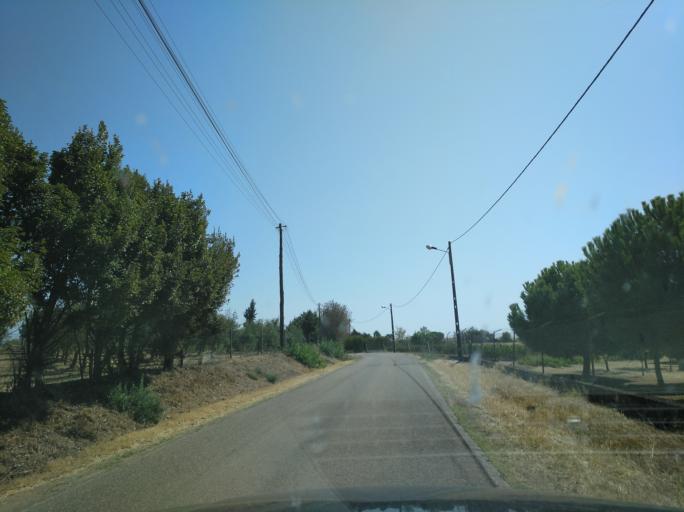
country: PT
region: Portalegre
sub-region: Campo Maior
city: Campo Maior
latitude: 39.0213
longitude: -7.0536
